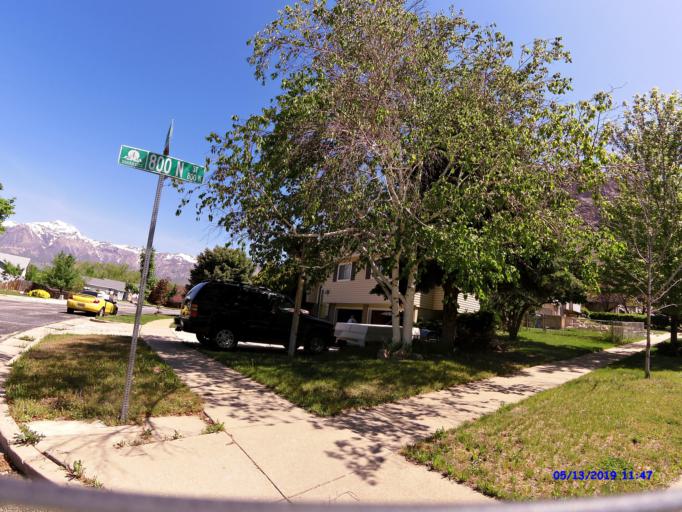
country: US
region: Utah
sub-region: Weber County
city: North Ogden
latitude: 41.2716
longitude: -111.9513
